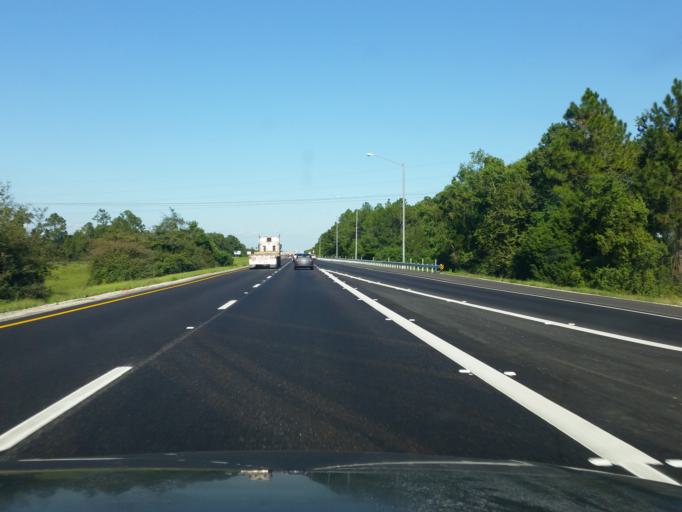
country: US
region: Mississippi
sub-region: Hancock County
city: Kiln
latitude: 30.3591
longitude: -89.4200
